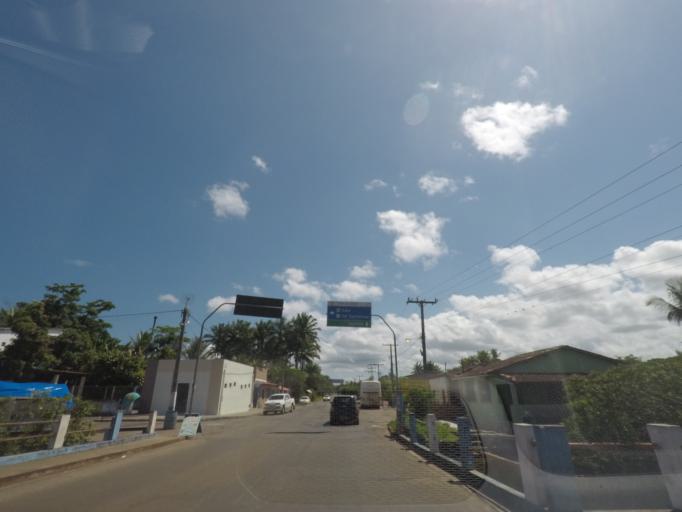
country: BR
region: Bahia
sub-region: Taperoa
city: Taperoa
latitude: -13.4812
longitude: -39.0906
